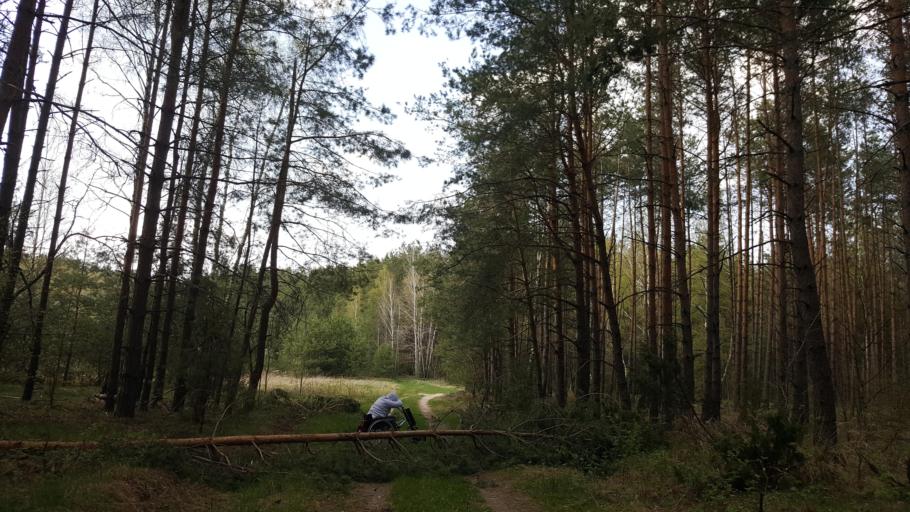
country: BY
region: Brest
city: Kamyanyets
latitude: 52.3505
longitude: 23.8413
